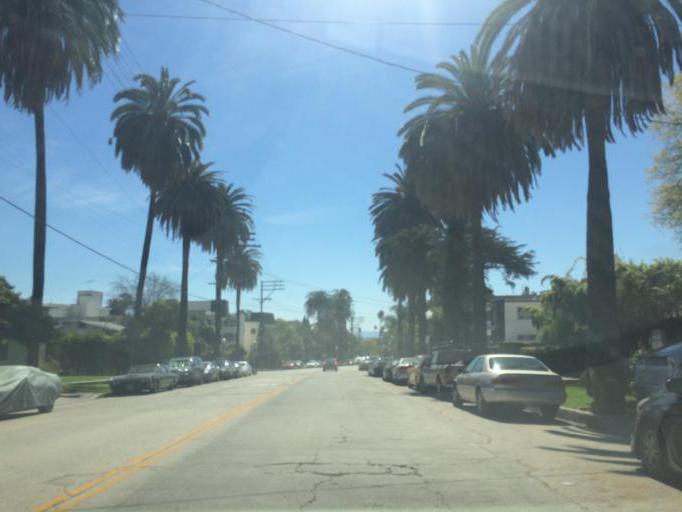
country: US
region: California
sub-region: Los Angeles County
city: Hollywood
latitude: 34.1098
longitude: -118.3215
